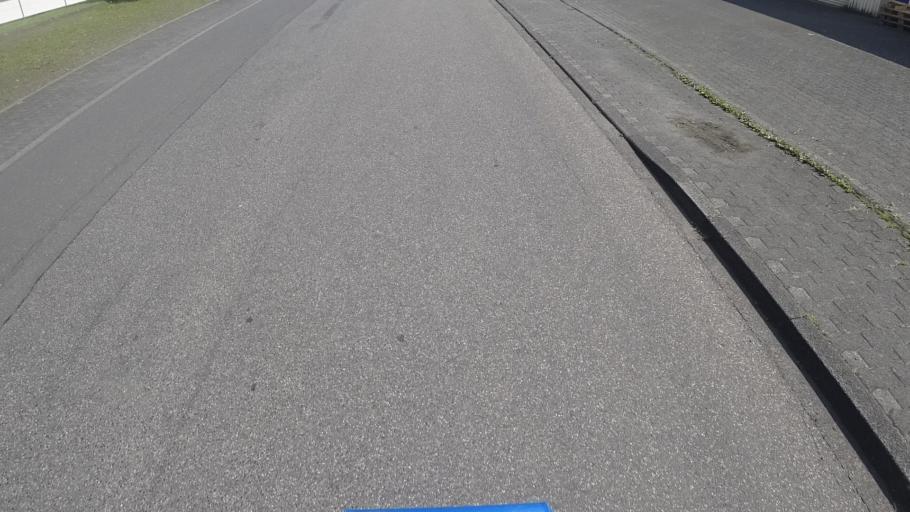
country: DE
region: Rheinland-Pfalz
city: Sankt Katharinen
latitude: 50.5926
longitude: 7.3626
